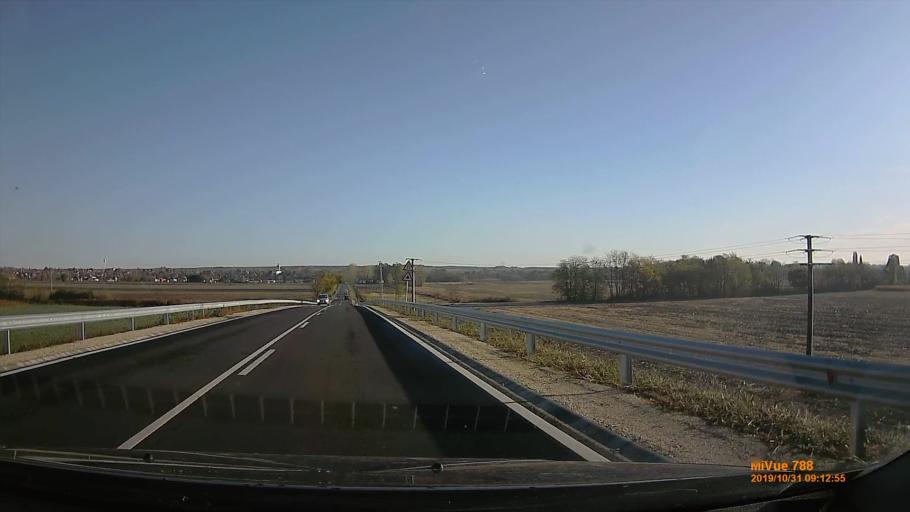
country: HU
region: Pest
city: Peteri
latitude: 47.3783
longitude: 19.4000
